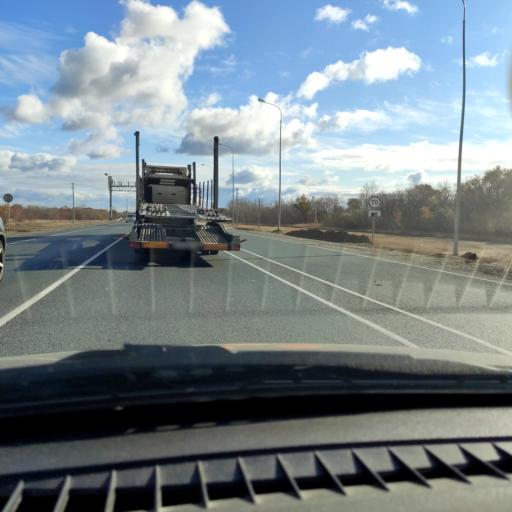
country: RU
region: Samara
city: Varlamovo
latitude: 53.1915
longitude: 48.3460
